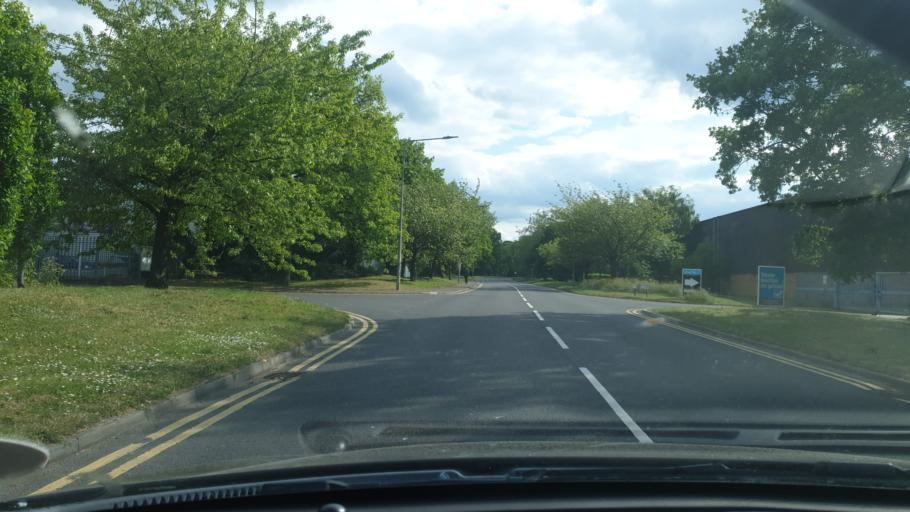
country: GB
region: England
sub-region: Essex
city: Colchester
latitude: 51.9180
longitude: 0.9293
